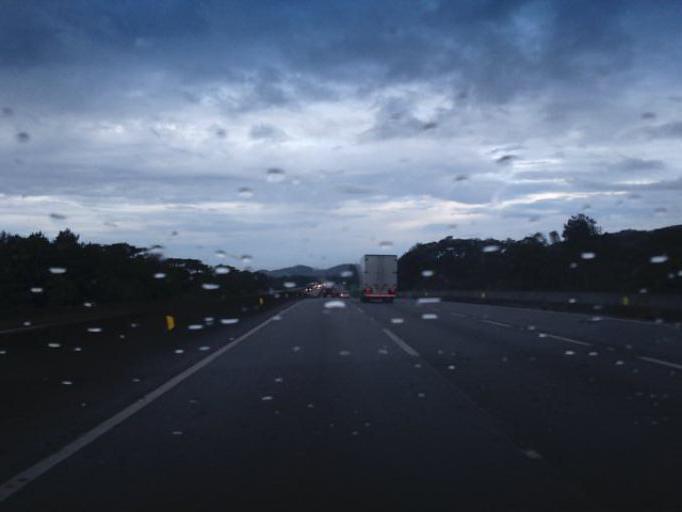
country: BR
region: Santa Catarina
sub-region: Joinville
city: Joinville
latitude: -26.0294
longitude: -48.8610
